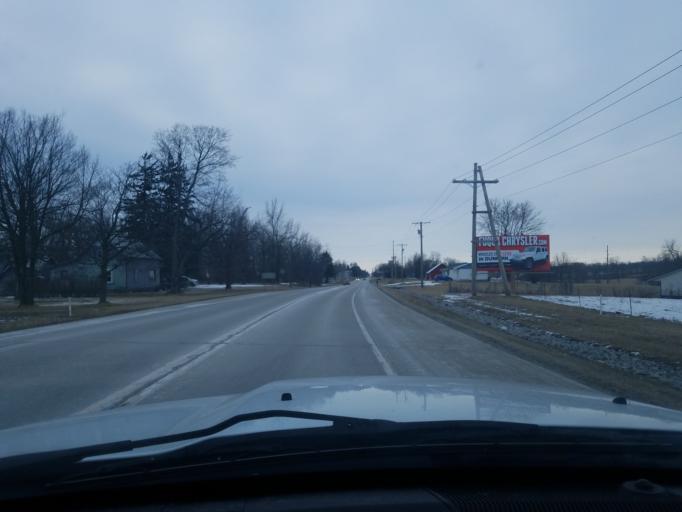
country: US
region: Indiana
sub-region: Randolph County
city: Farmland
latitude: 40.1763
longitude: -85.1276
